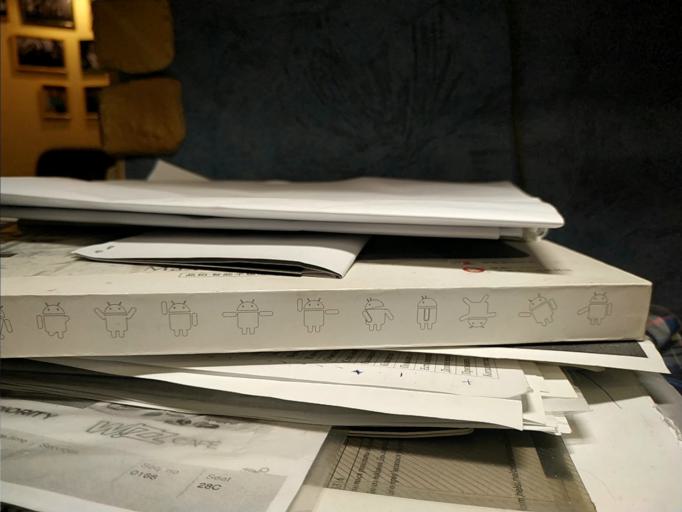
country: RU
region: Tverskaya
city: Zubtsov
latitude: 56.0852
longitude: 34.7740
